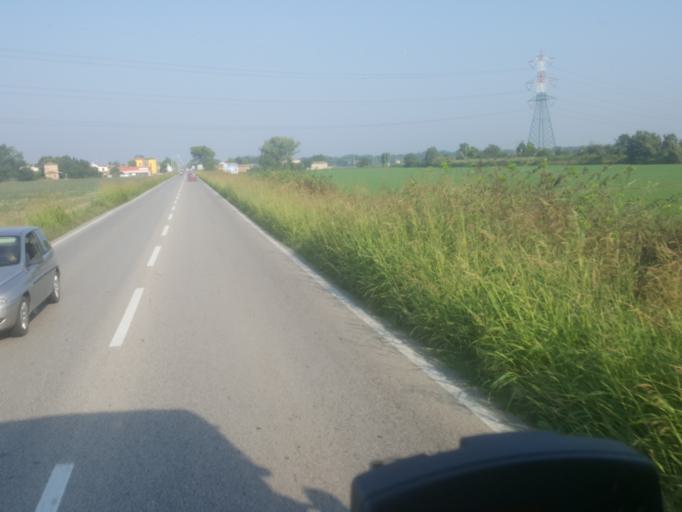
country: IT
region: Emilia-Romagna
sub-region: Provincia di Ravenna
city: Fornace Zarattini
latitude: 44.4457
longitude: 12.1304
